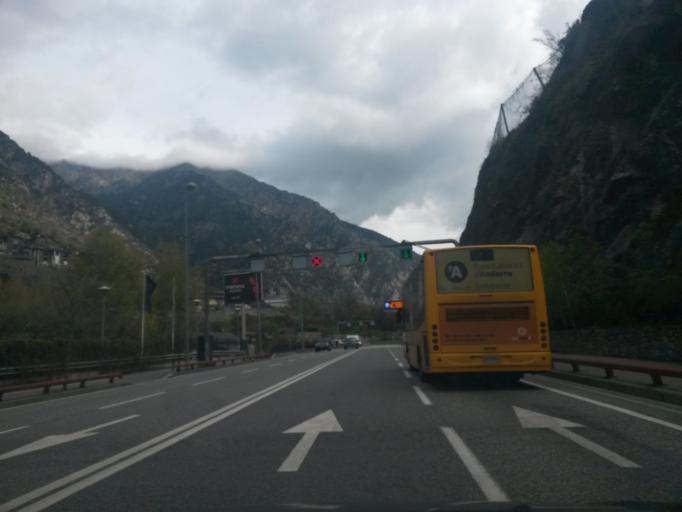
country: AD
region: Sant Julia de Loria
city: Sant Julia de Loria
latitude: 42.4827
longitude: 1.4902
